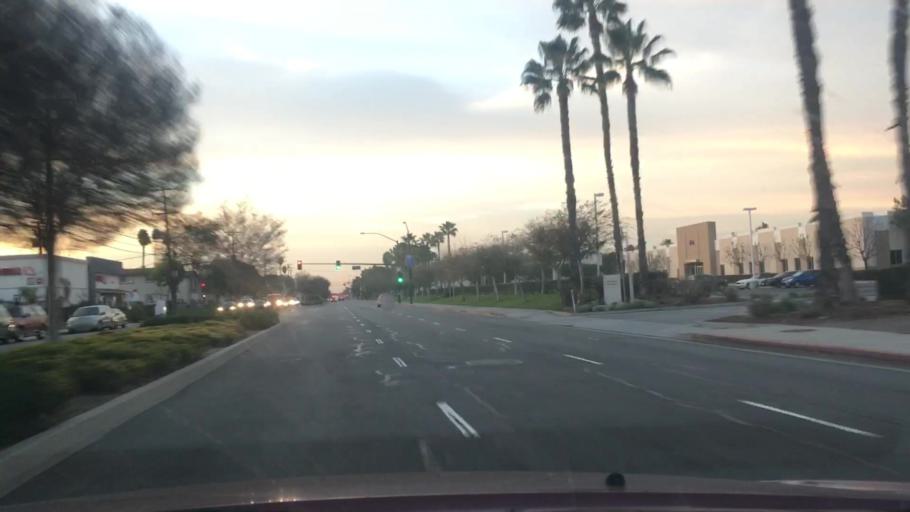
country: US
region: California
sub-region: Orange County
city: Buena Park
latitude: 33.8662
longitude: -118.0114
